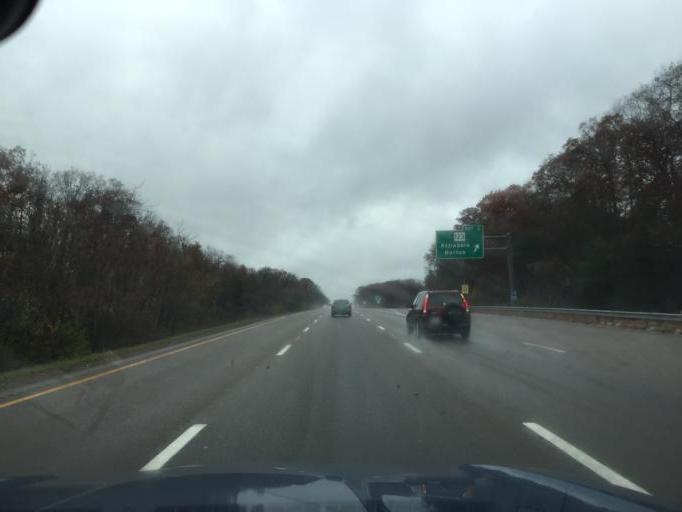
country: US
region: Massachusetts
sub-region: Bristol County
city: Attleboro
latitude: 41.9295
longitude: -71.3226
